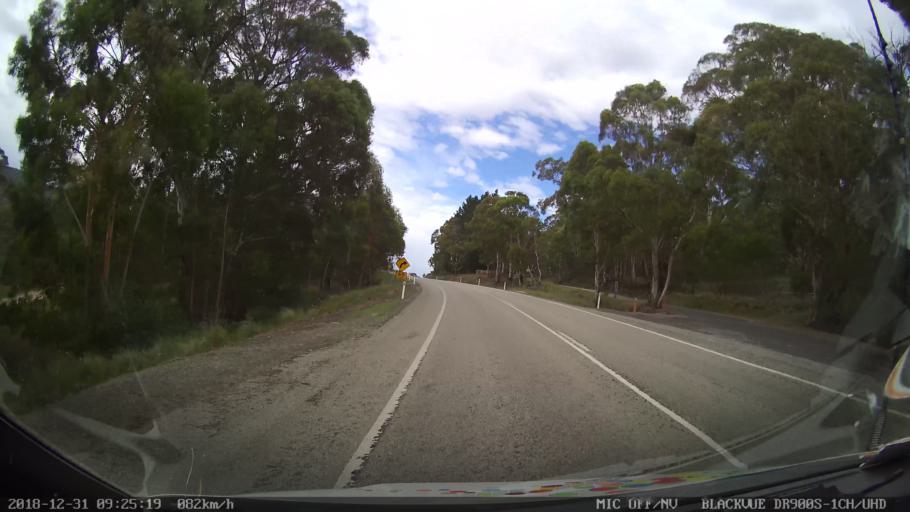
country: AU
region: New South Wales
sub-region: Snowy River
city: Jindabyne
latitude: -36.4423
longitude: 148.5087
